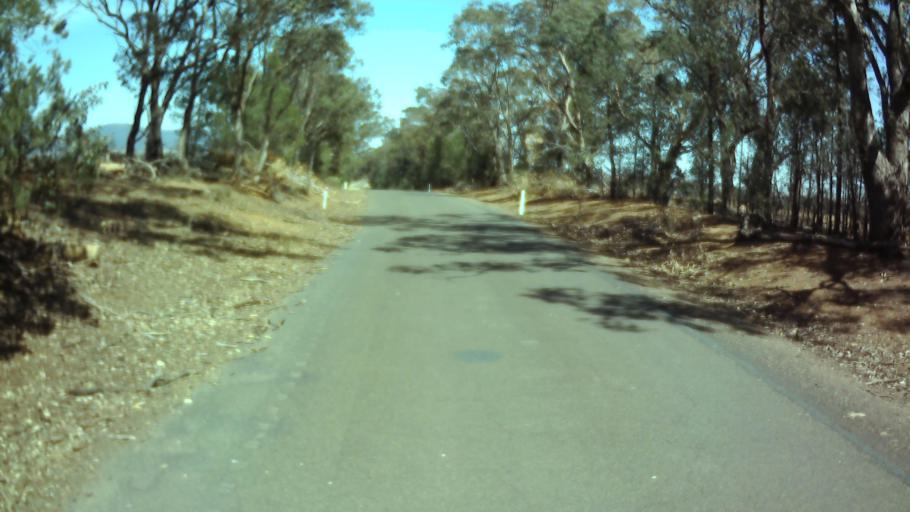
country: AU
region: New South Wales
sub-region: Weddin
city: Grenfell
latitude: -33.8706
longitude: 148.0969
